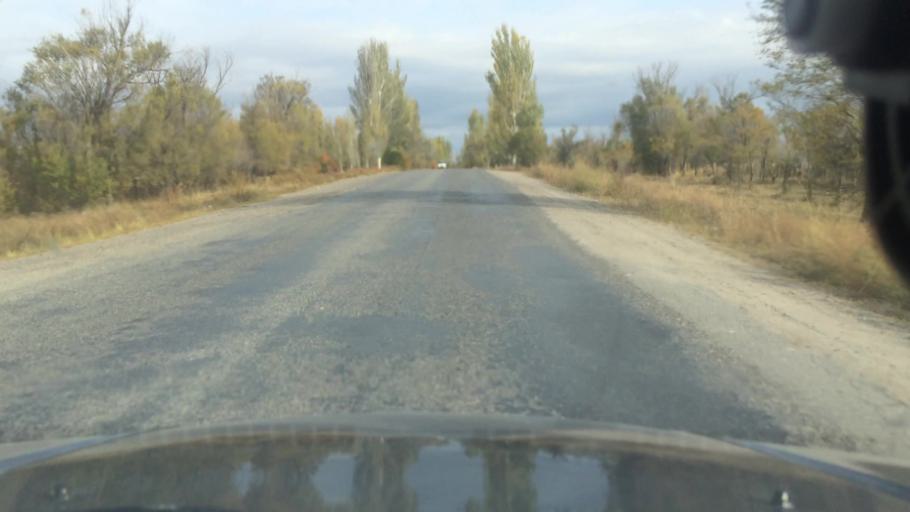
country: KG
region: Ysyk-Koel
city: Karakol
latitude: 42.5687
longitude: 78.3911
